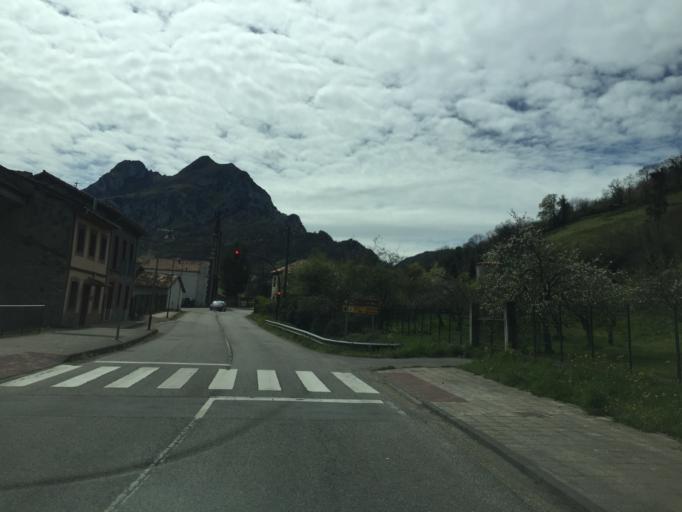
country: ES
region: Asturias
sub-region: Province of Asturias
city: Proaza
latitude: 43.2574
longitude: -6.0117
